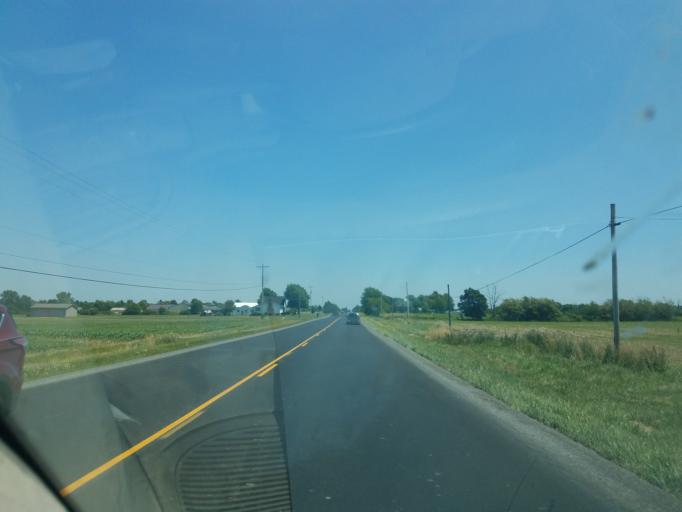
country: US
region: Ohio
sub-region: Hardin County
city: Ada
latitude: 40.7323
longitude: -83.9054
